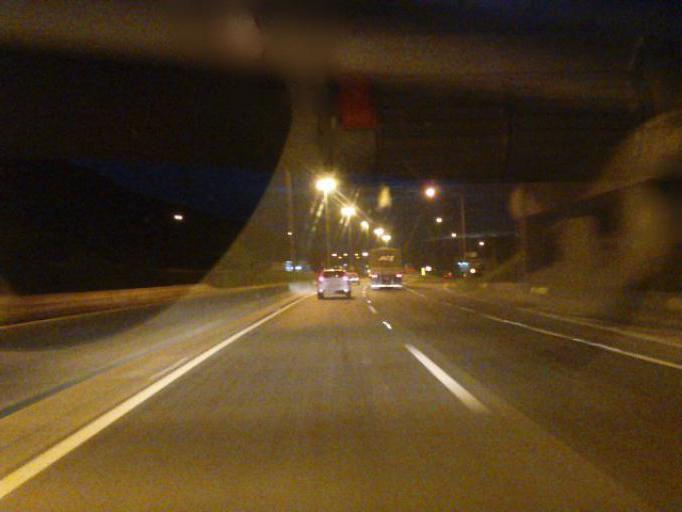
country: BR
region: Santa Catarina
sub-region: Penha
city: Penha
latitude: -26.8064
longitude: -48.6802
